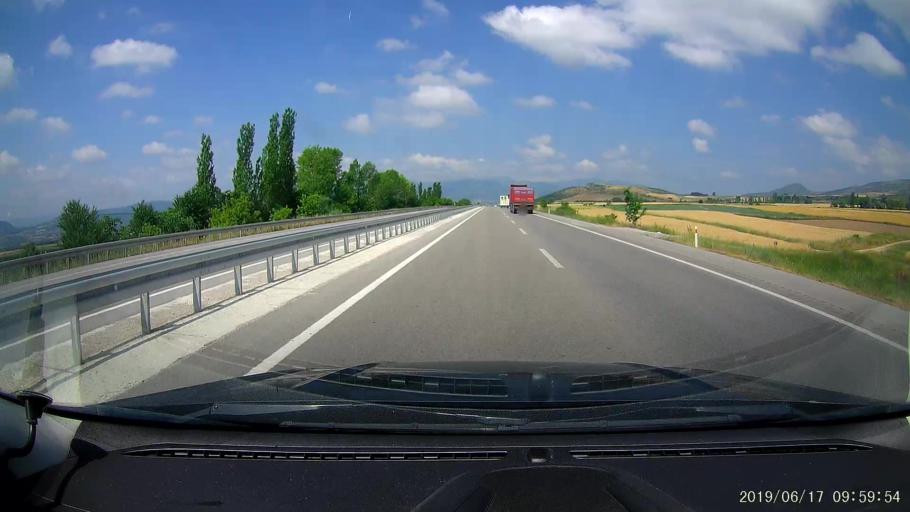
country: TR
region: Amasya
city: Alicik
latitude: 40.8664
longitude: 35.3022
